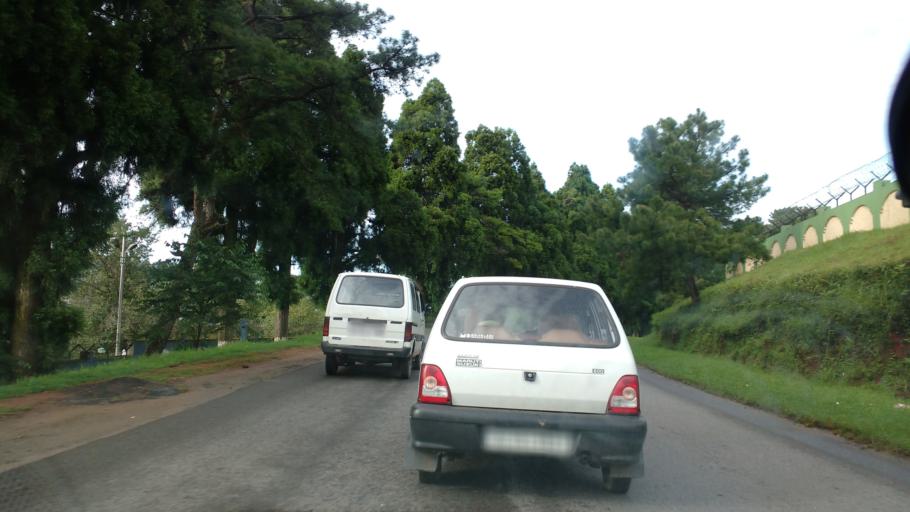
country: IN
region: Meghalaya
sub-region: East Khasi Hills
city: Shillong
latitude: 25.5406
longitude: 91.8292
